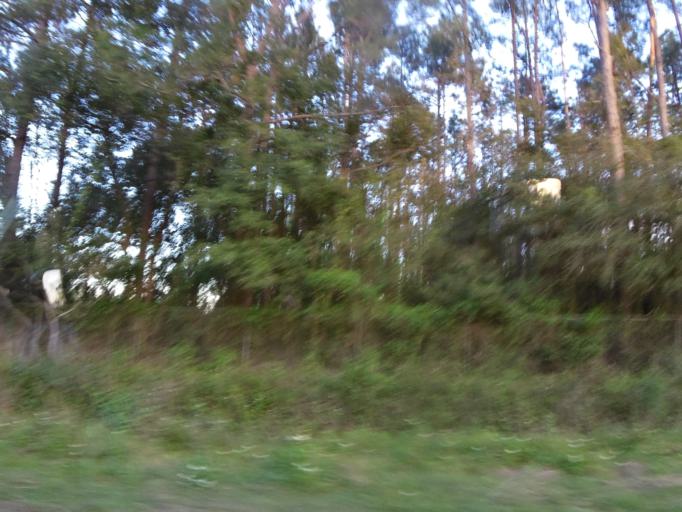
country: US
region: Florida
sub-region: Duval County
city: Jacksonville
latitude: 30.3466
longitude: -81.7292
